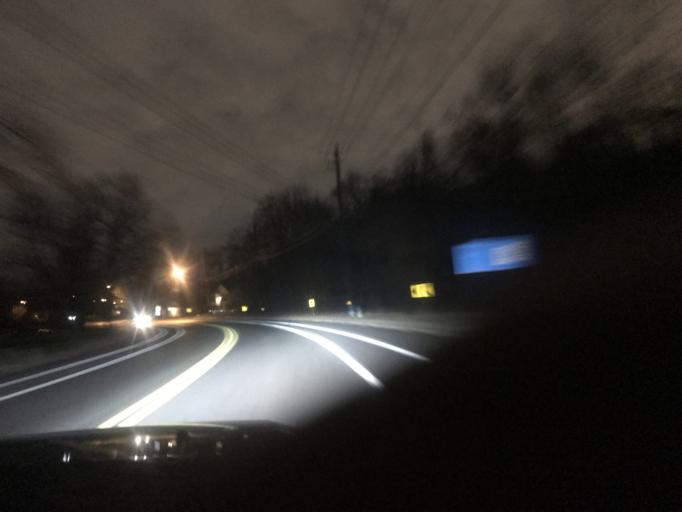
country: US
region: Maryland
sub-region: Prince George's County
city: Hillcrest Heights
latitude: 38.8175
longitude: -76.9720
